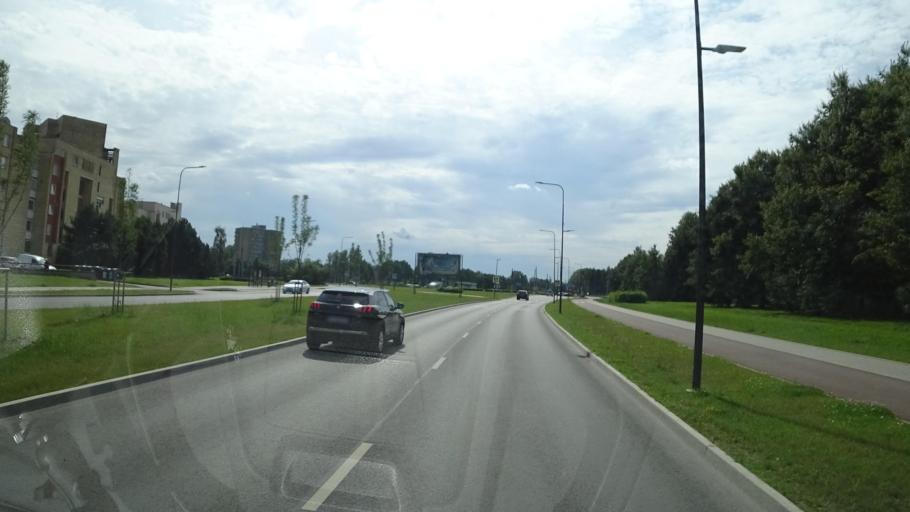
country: LT
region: Kauno apskritis
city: Dainava (Kaunas)
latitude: 54.9145
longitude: 23.9780
